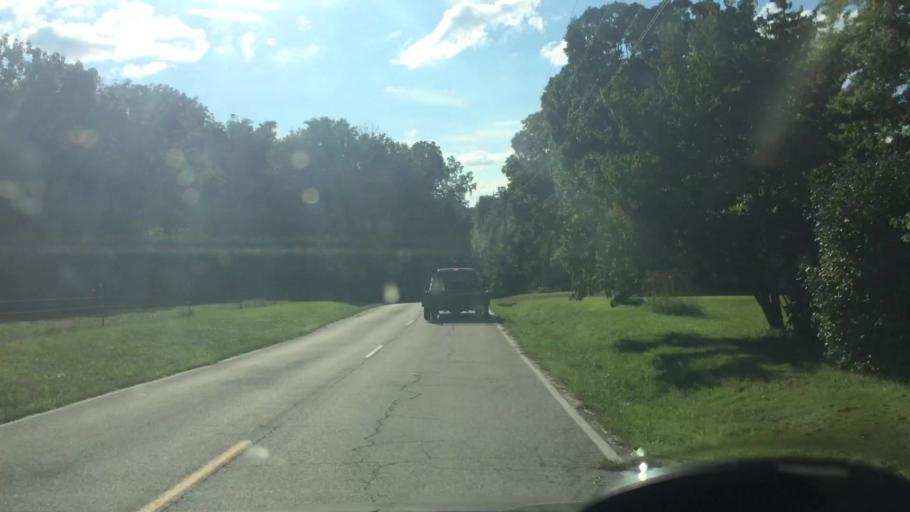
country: US
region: Missouri
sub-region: Greene County
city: Strafford
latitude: 37.2846
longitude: -93.0842
